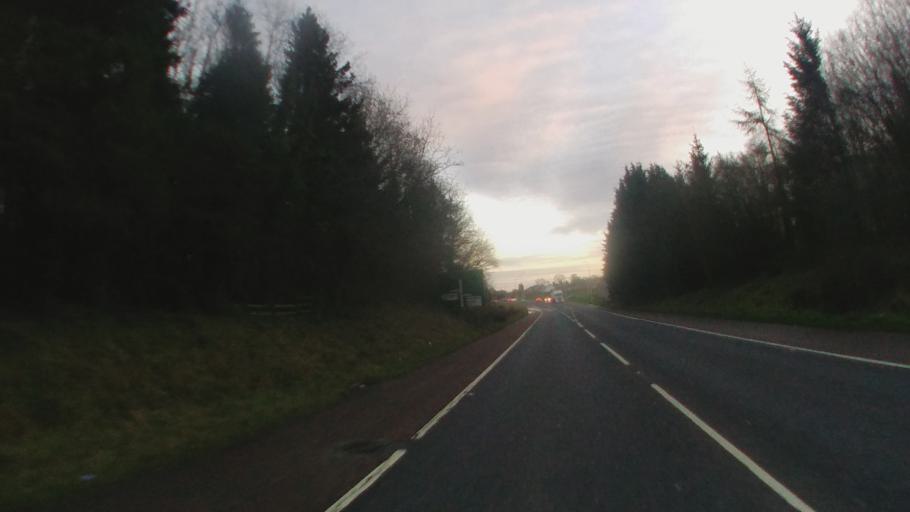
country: GB
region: Northern Ireland
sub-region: Armagh District
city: Tandragee
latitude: 54.2988
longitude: -6.5177
